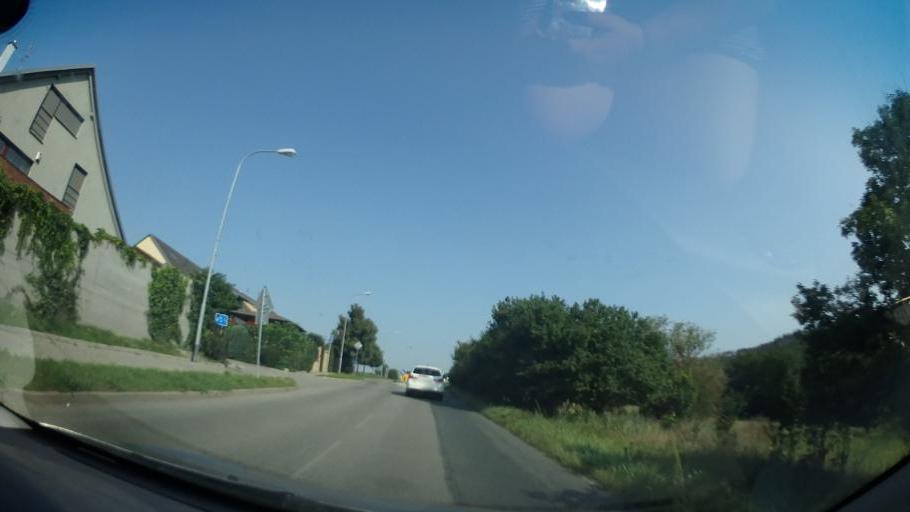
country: CZ
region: South Moravian
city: Kurim
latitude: 49.2396
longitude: 16.5305
